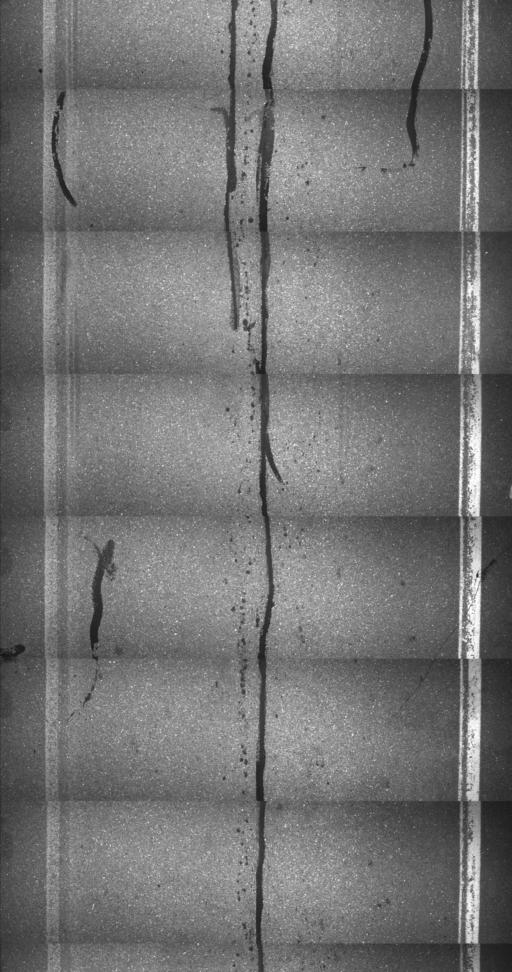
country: US
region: Vermont
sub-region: Orleans County
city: Newport
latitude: 44.9847
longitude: -72.3608
